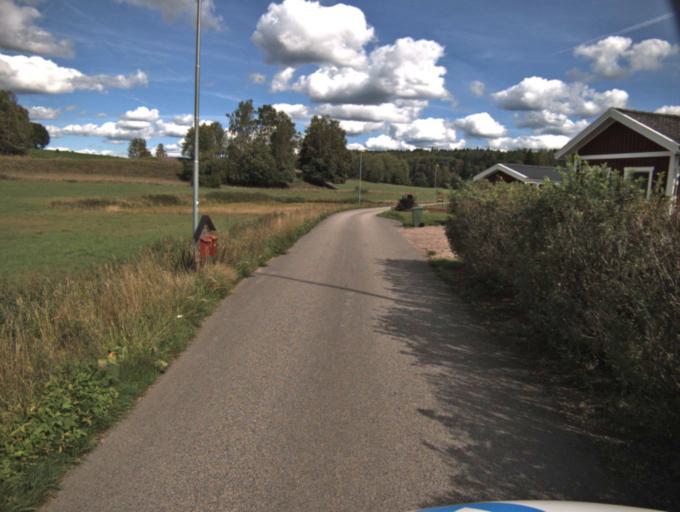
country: SE
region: Vaestra Goetaland
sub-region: Ulricehamns Kommun
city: Ulricehamn
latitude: 57.9309
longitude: 13.5018
